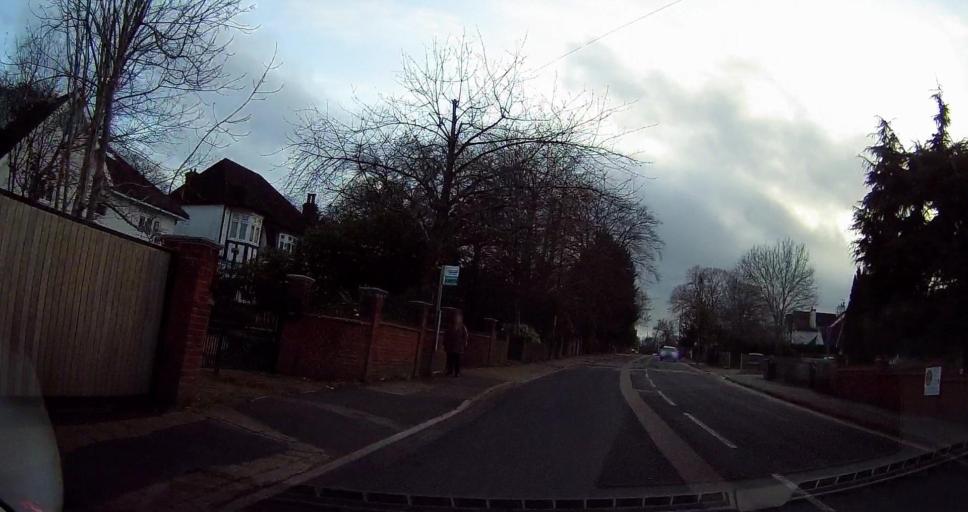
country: GB
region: England
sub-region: Kent
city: Chatham
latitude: 51.3625
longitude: 0.5182
